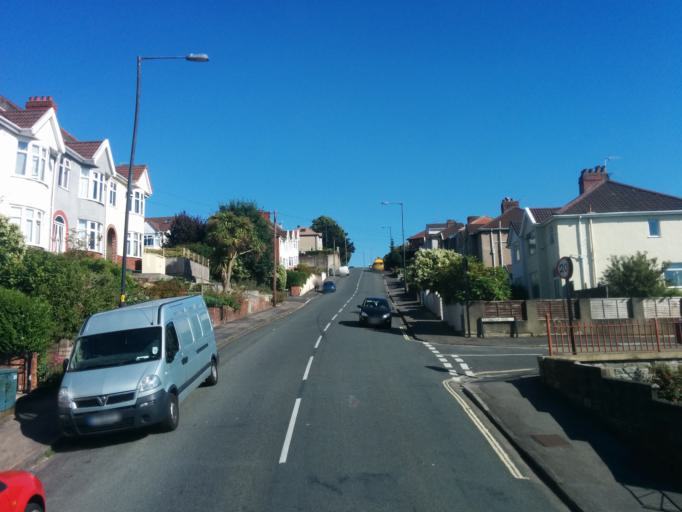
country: GB
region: England
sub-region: Bristol
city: Bristol
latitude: 51.4361
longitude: -2.5813
